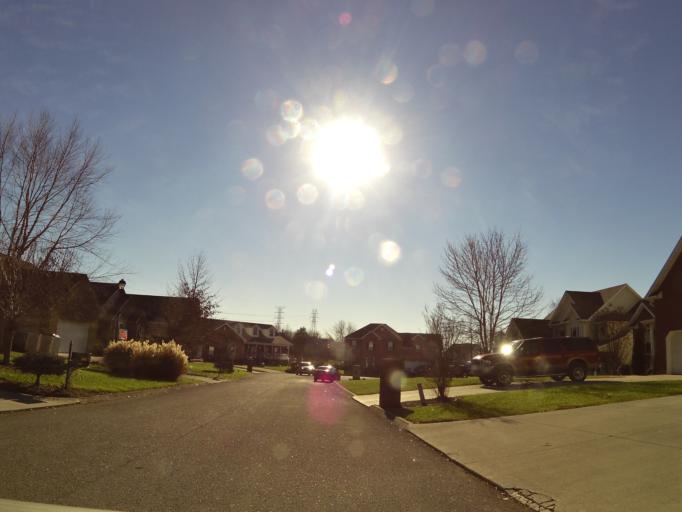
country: US
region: Tennessee
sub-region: Knox County
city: Knoxville
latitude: 36.0384
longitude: -83.9674
